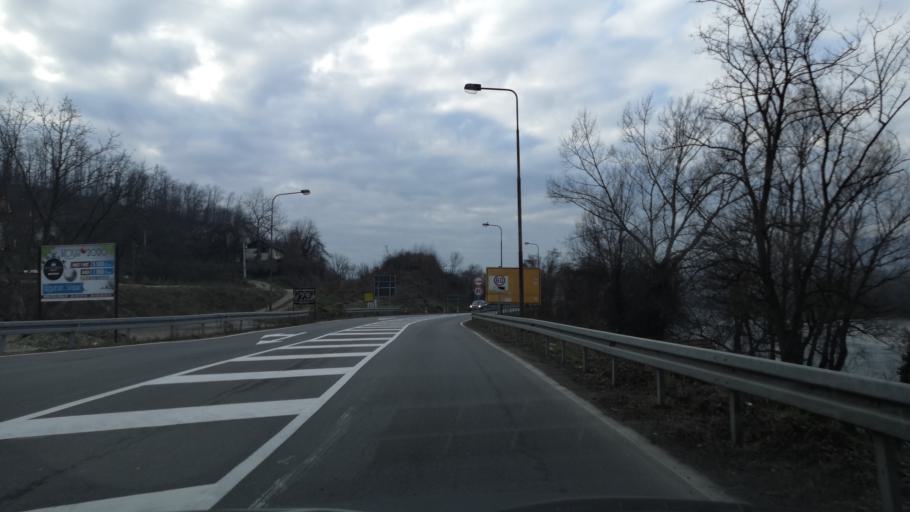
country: BA
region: Republika Srpska
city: Petkovci
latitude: 44.5135
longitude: 19.1286
